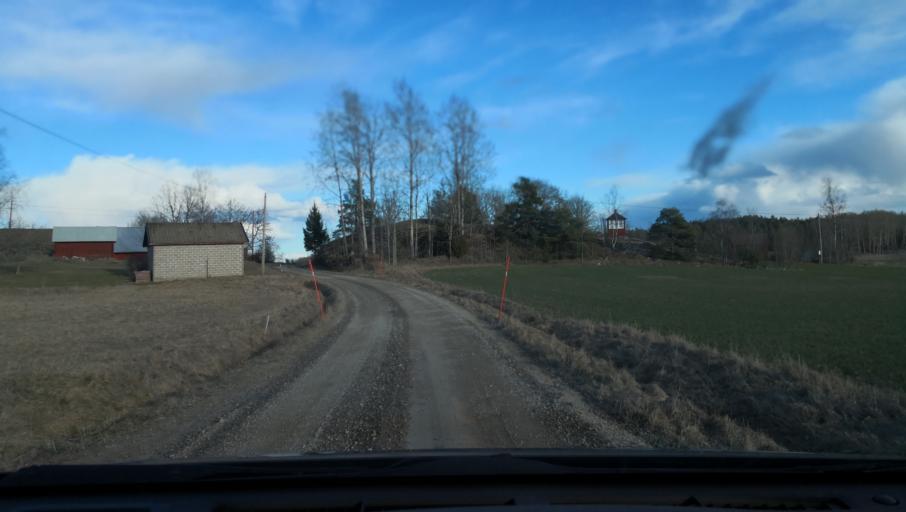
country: SE
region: Vaestmanland
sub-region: Arboga Kommun
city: Arboga
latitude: 59.4475
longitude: 15.7418
